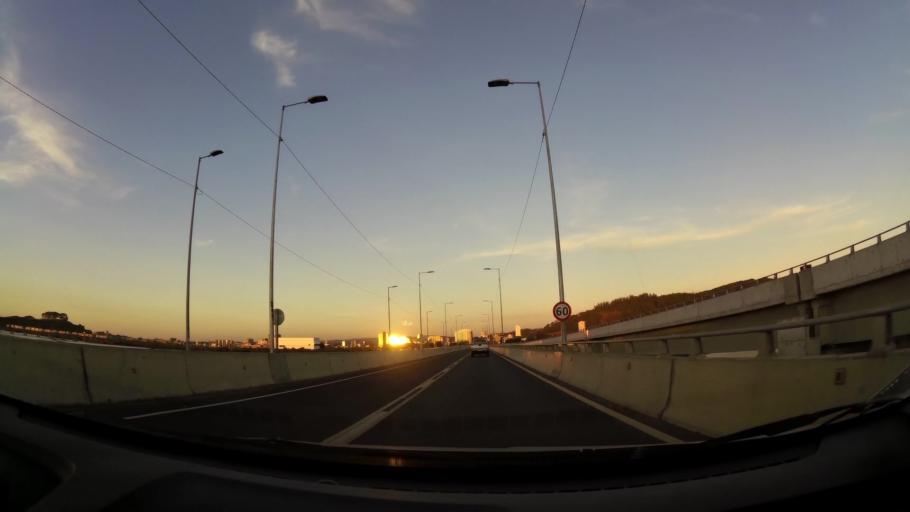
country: CL
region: Biobio
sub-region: Provincia de Concepcion
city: Concepcion
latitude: -36.8408
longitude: -73.0717
